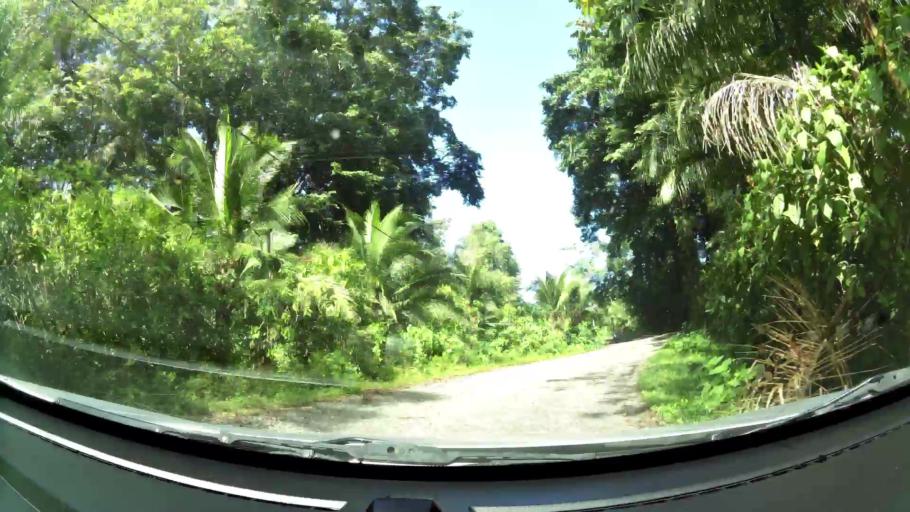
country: PA
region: Bocas del Toro
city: Barranco
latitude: 9.6391
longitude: -82.6912
